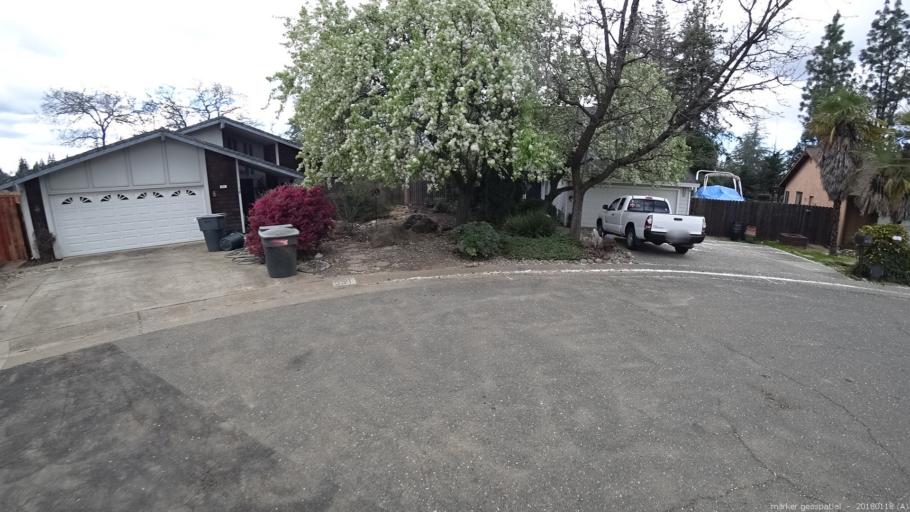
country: US
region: California
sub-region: Sacramento County
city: Orangevale
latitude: 38.6666
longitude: -121.2080
